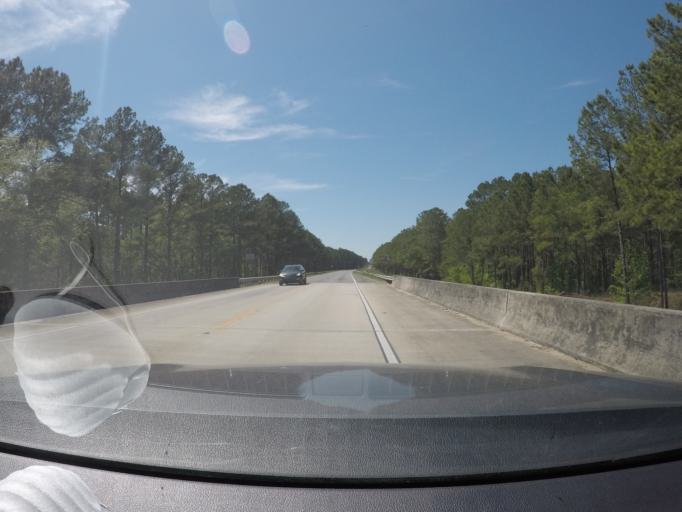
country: US
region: Georgia
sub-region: Evans County
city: Claxton
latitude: 32.1485
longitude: -81.7818
